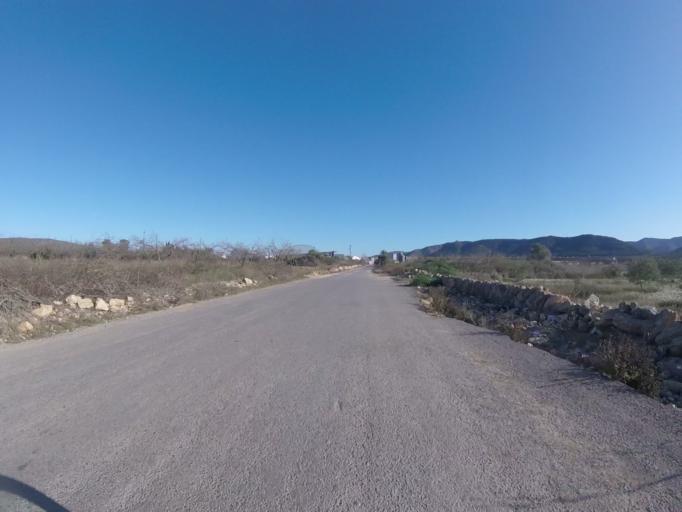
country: ES
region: Valencia
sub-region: Provincia de Castello
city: Alcala de Xivert
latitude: 40.2975
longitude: 0.2194
